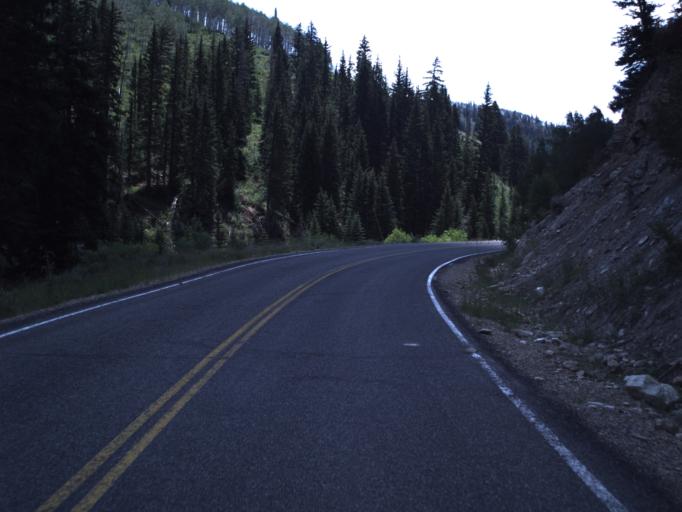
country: US
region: Utah
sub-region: Sanpete County
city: Fairview
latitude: 39.6738
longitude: -111.1552
